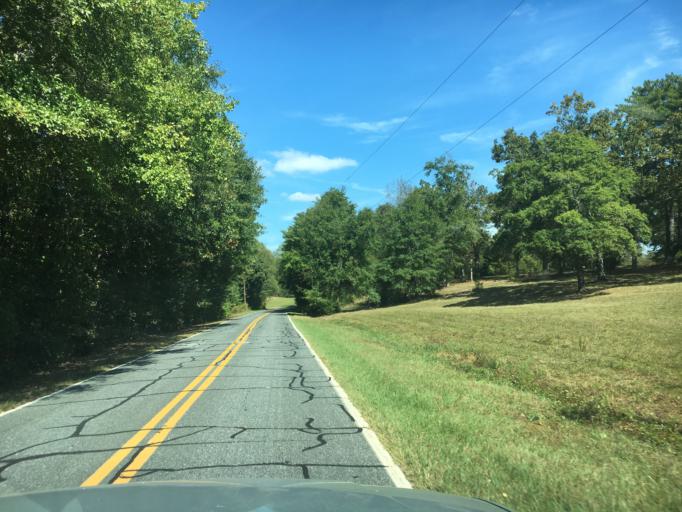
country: US
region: South Carolina
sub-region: Spartanburg County
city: Mayo
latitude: 35.1906
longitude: -81.9235
